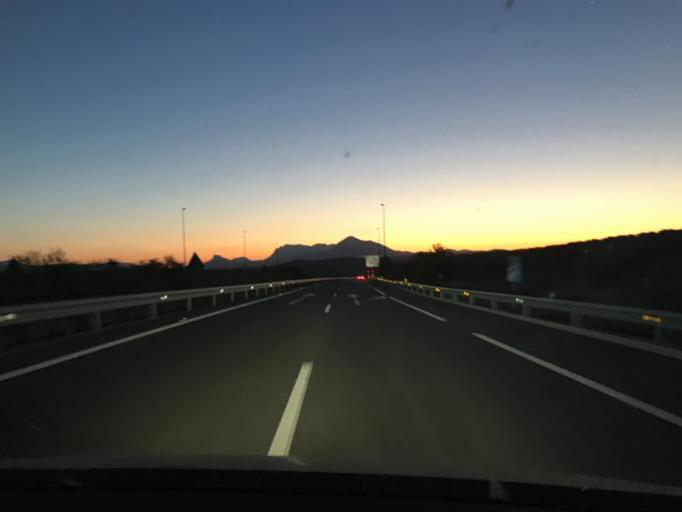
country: ES
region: Andalusia
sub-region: Province of Cordoba
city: Encinas Reales
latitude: 37.2816
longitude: -4.4927
